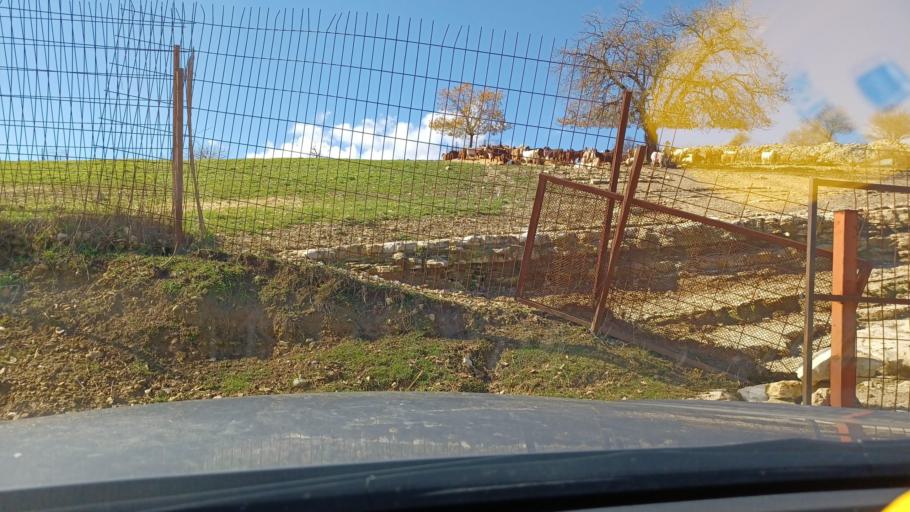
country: CY
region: Limassol
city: Pachna
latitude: 34.8244
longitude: 32.7795
